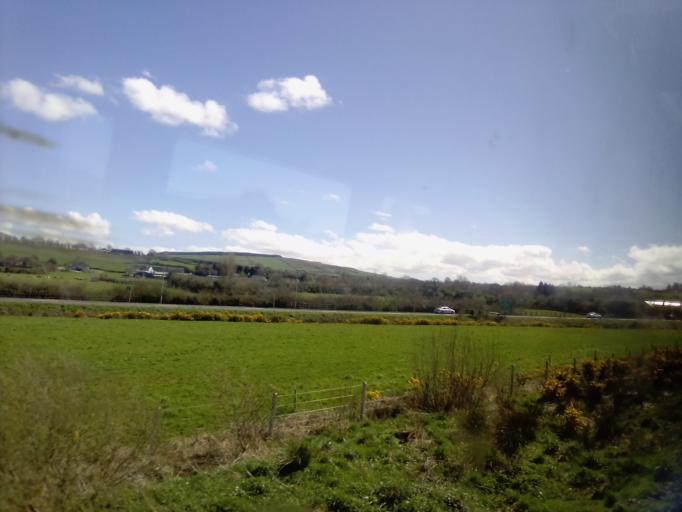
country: IE
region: Munster
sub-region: Ciarrai
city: Castleisland
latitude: 52.1764
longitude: -9.5488
